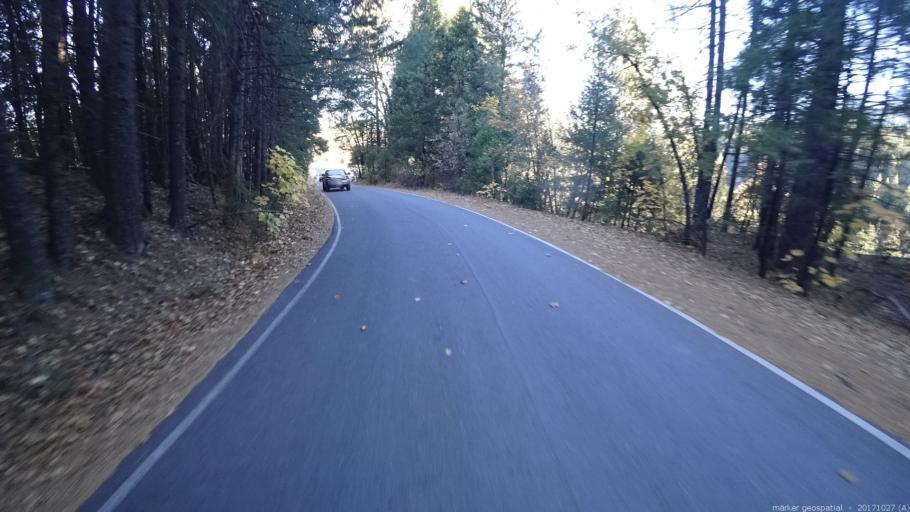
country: US
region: California
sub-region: Shasta County
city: Burney
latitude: 40.9998
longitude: -121.8863
